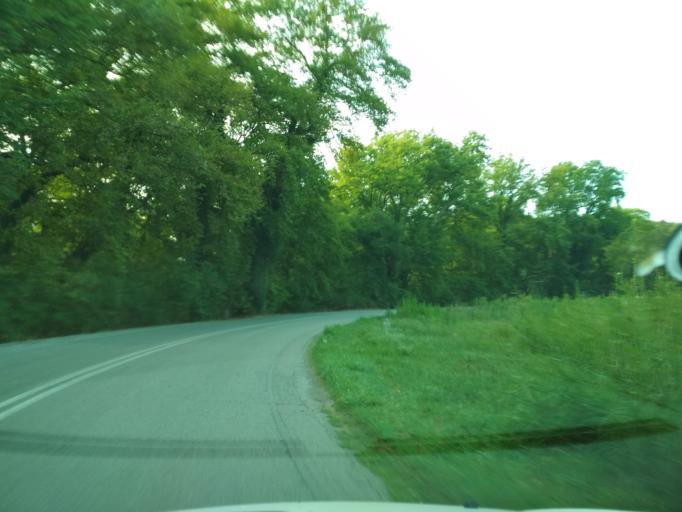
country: GR
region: Central Greece
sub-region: Nomos Evvoias
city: Mantoudi
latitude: 38.7667
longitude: 23.4779
